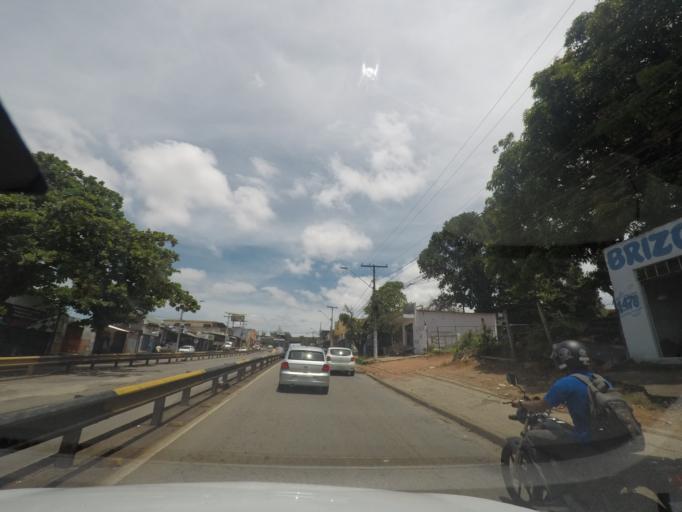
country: BR
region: Goias
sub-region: Goiania
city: Goiania
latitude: -16.6694
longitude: -49.2249
